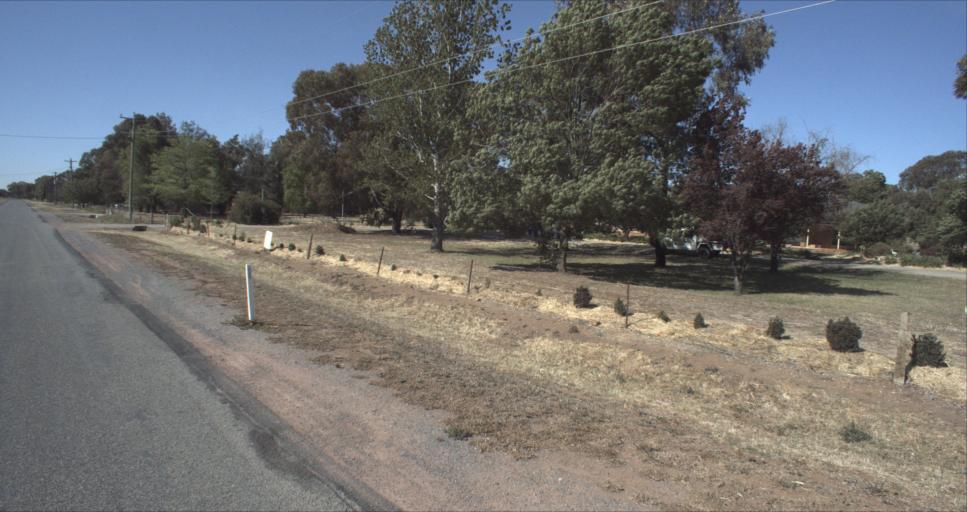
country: AU
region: New South Wales
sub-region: Leeton
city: Leeton
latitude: -34.5417
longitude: 146.4189
